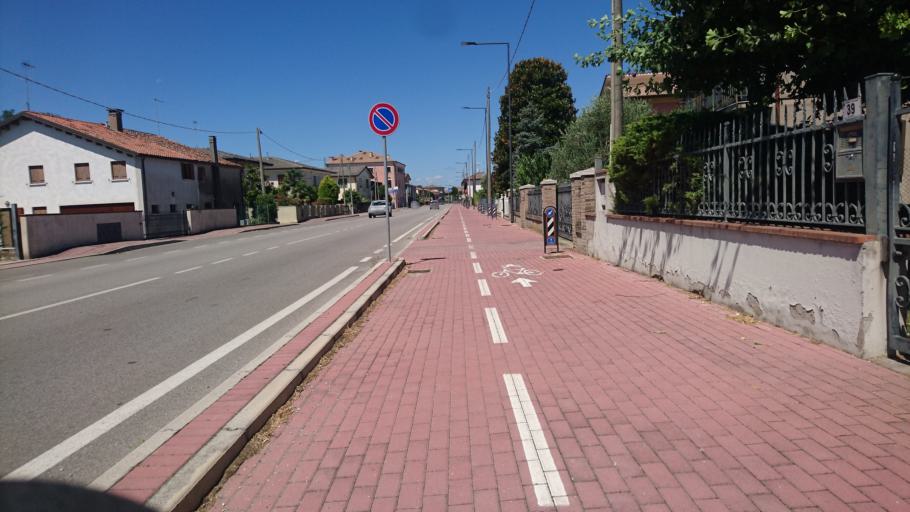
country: IT
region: Veneto
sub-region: Provincia di Padova
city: Campagnola
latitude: 45.2765
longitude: 12.0047
